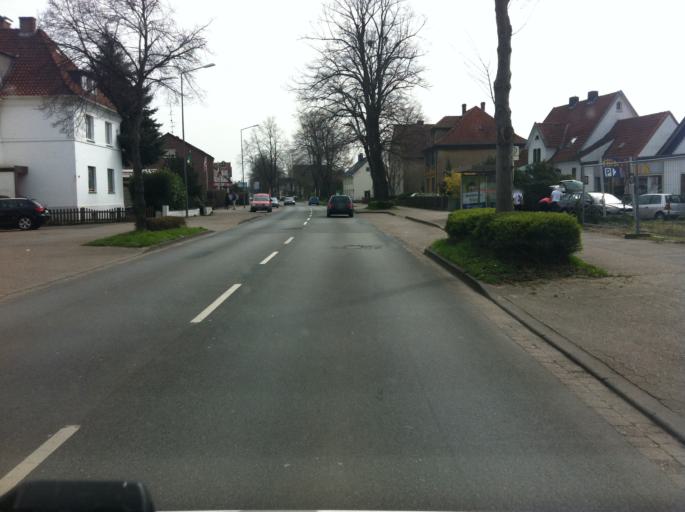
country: DE
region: North Rhine-Westphalia
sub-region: Regierungsbezirk Detmold
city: Minden
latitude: 52.2903
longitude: 8.8889
